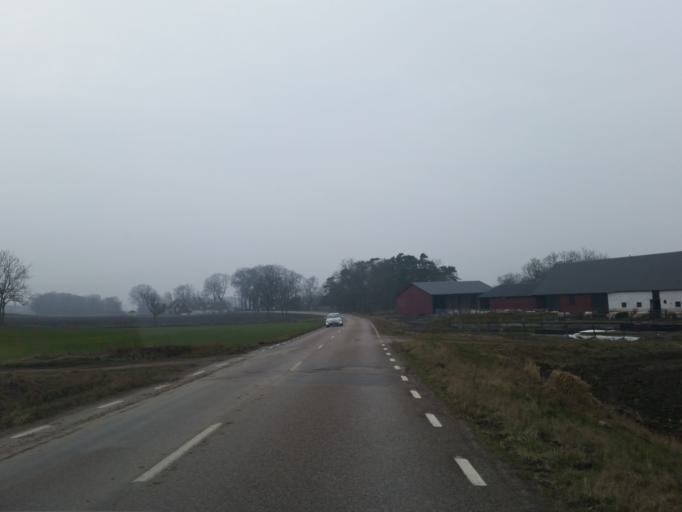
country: SE
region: Kalmar
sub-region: Morbylanga Kommun
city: Moerbylanga
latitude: 56.4236
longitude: 16.4149
